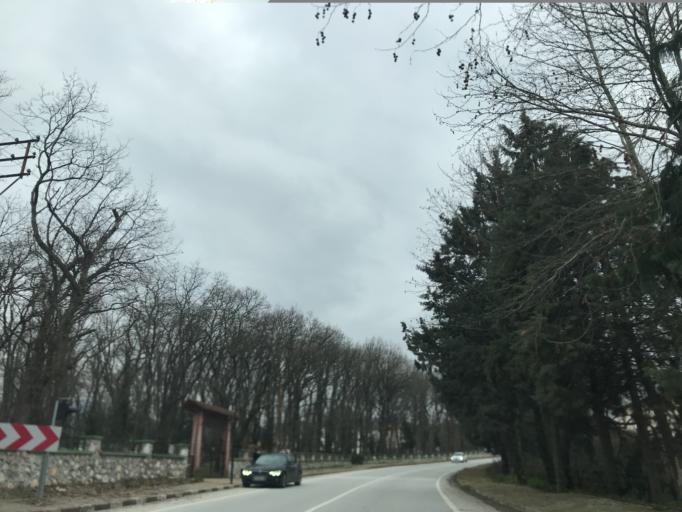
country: TR
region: Yalova
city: Kadikoy
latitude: 40.6082
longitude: 29.2032
